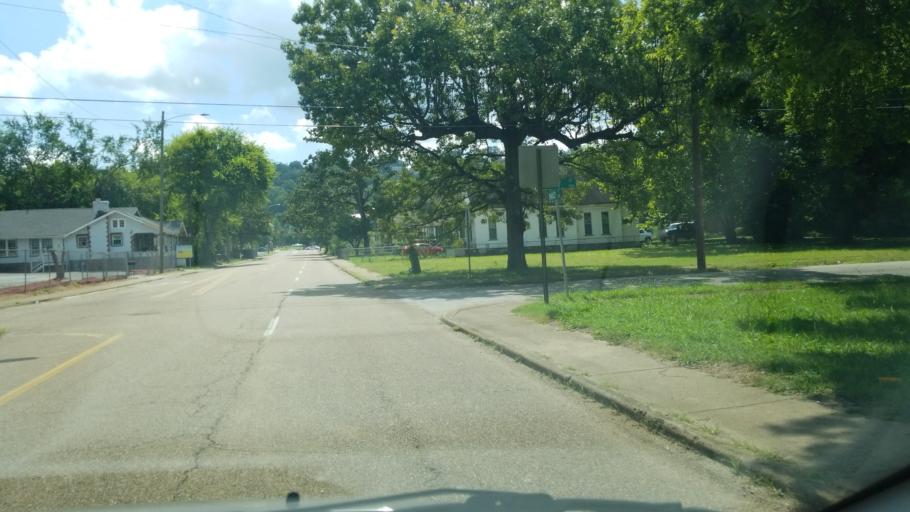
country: US
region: Tennessee
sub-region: Hamilton County
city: East Ridge
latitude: 35.0302
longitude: -85.2677
